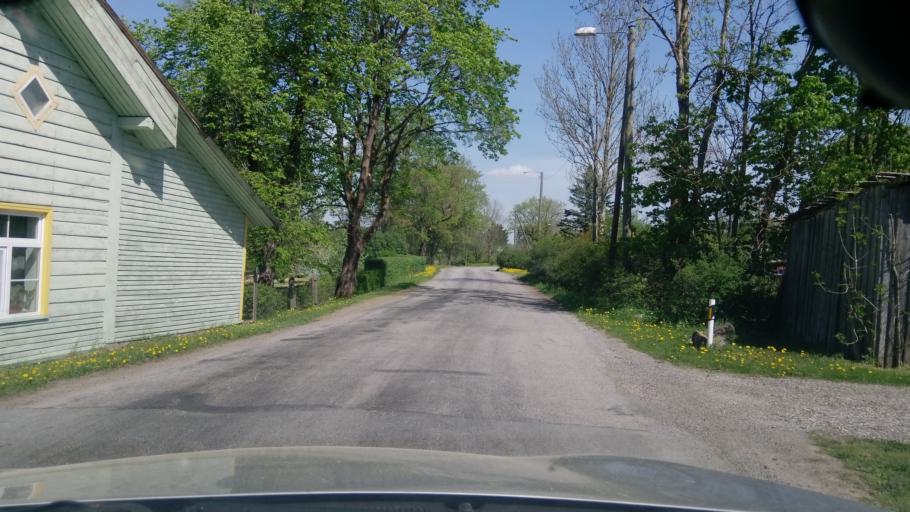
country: EE
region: Laeaene-Virumaa
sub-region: Tapa vald
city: Tapa
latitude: 59.1923
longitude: 25.8390
